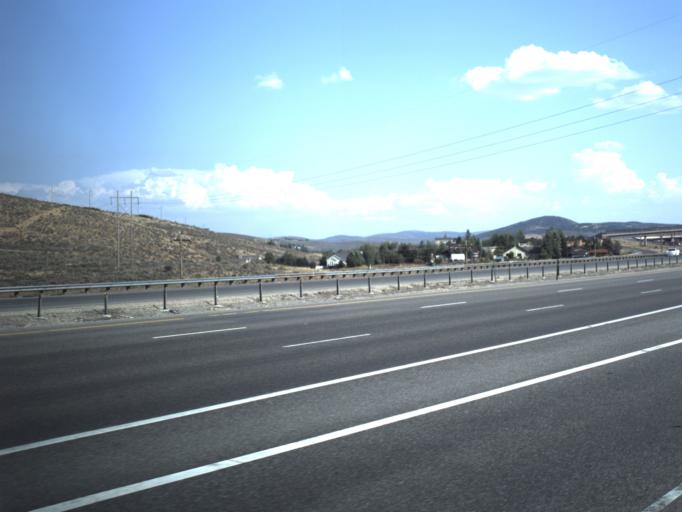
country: US
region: Utah
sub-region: Summit County
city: Snyderville
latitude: 40.7322
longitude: -111.5514
